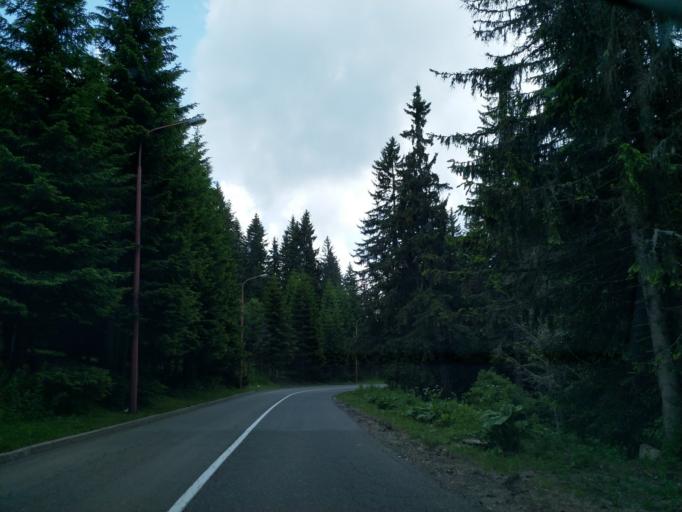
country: XK
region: Mitrovica
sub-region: Komuna e Leposaviqit
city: Leposaviq
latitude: 43.2853
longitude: 20.7969
